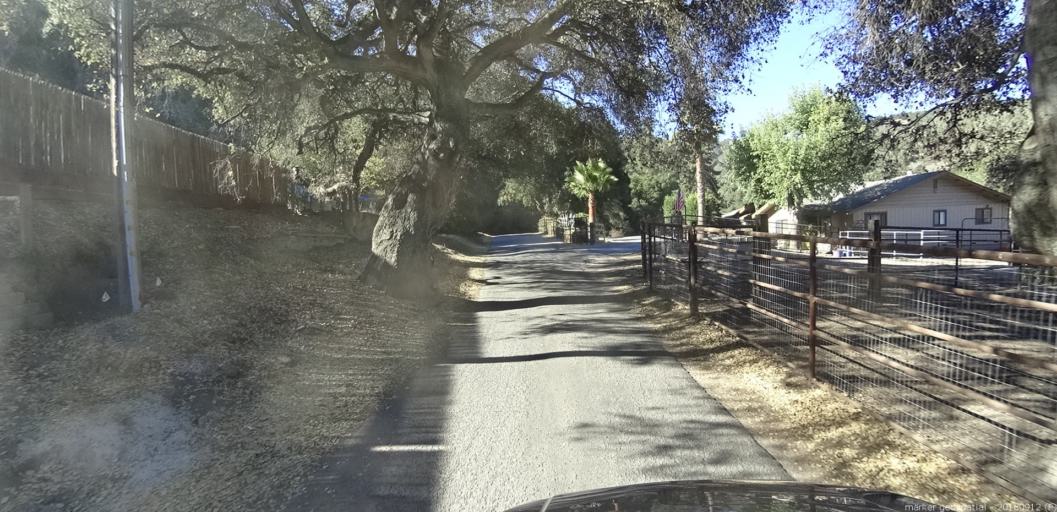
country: US
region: California
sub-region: Monterey County
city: Carmel Valley Village
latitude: 36.5399
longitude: -121.7363
